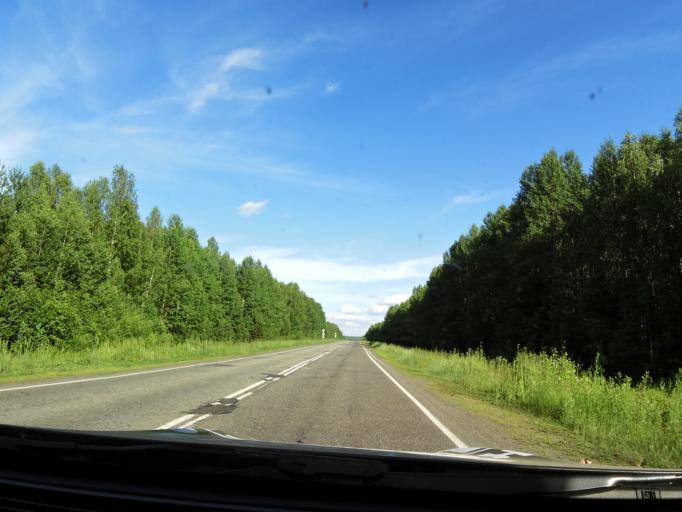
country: RU
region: Kirov
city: Dubrovka
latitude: 58.8974
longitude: 51.3186
